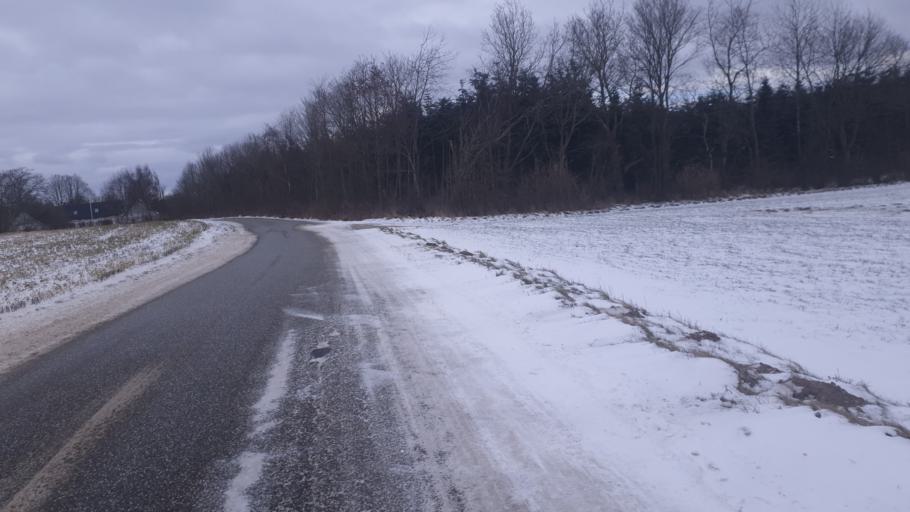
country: DK
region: Central Jutland
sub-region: Hedensted Kommune
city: Hedensted
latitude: 55.7961
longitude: 9.7064
